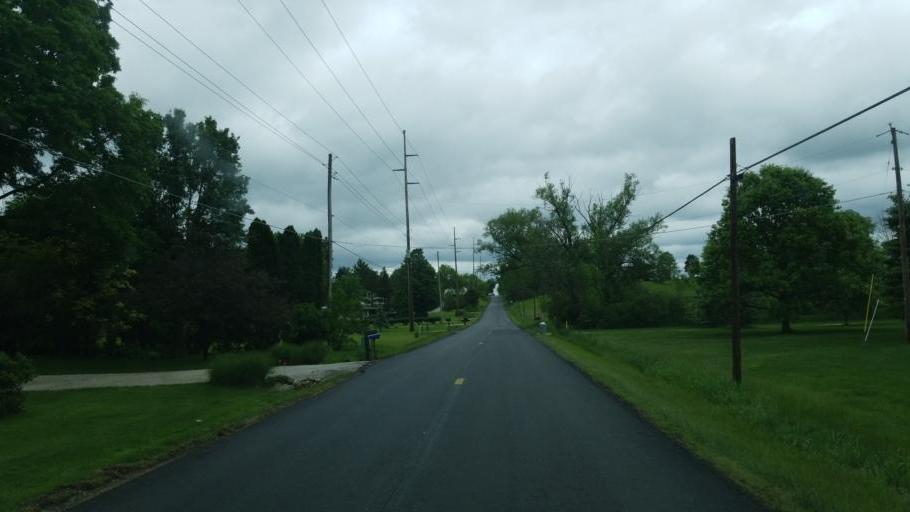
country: US
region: Ohio
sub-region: Medina County
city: Brunswick
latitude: 41.1997
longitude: -81.8782
